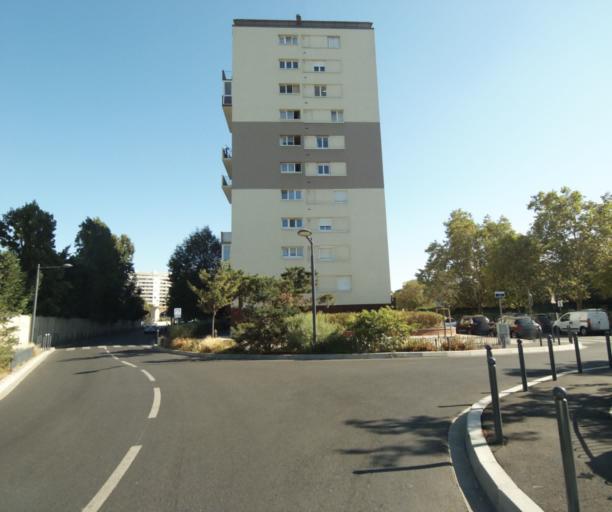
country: FR
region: Ile-de-France
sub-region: Departement des Hauts-de-Seine
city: Villeneuve-la-Garenne
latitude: 48.9399
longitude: 2.3317
